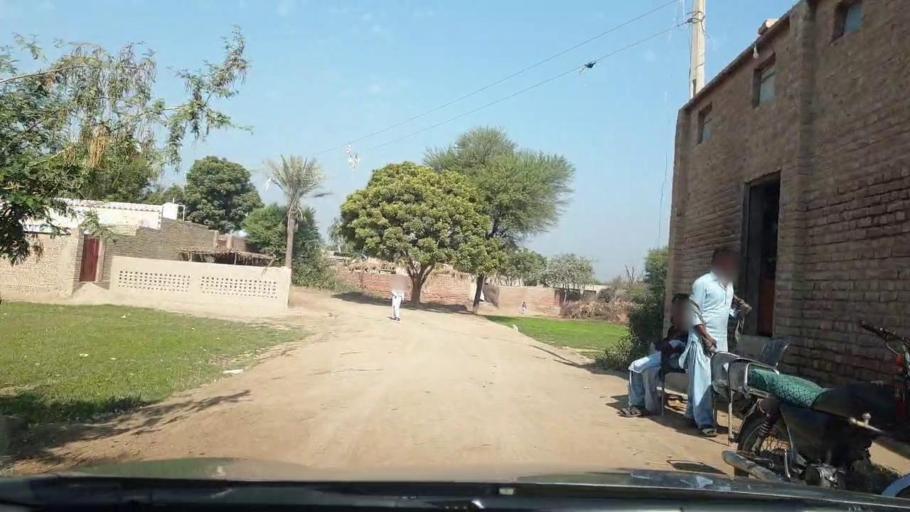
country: PK
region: Sindh
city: Tando Allahyar
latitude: 25.4641
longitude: 68.6678
